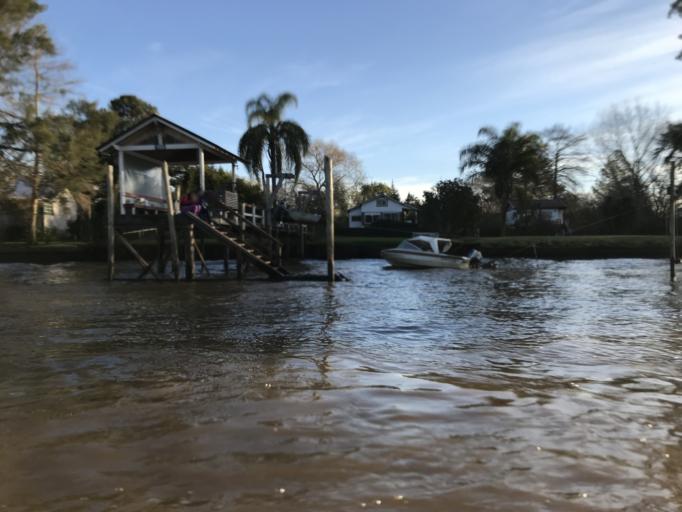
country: AR
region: Buenos Aires
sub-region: Partido de Tigre
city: Tigre
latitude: -34.3916
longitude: -58.5743
